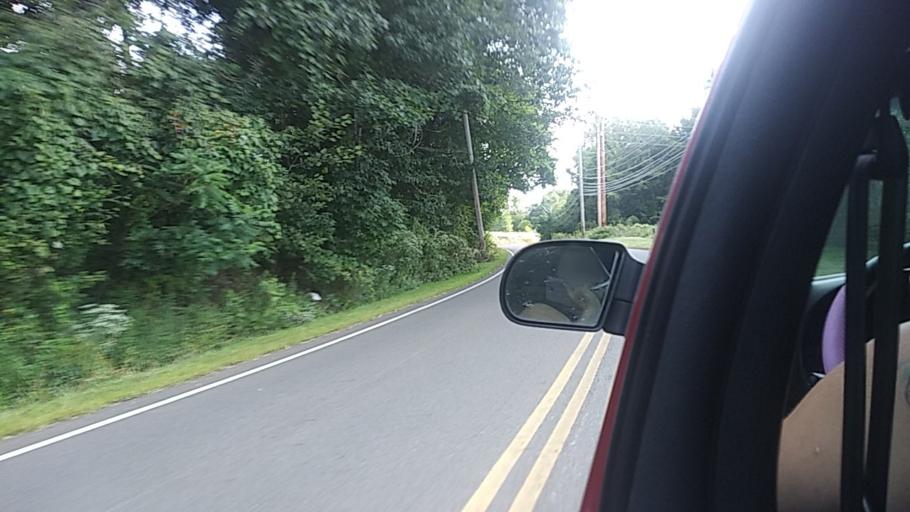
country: US
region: Ohio
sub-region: Summit County
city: Tallmadge
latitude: 41.0933
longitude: -81.4742
